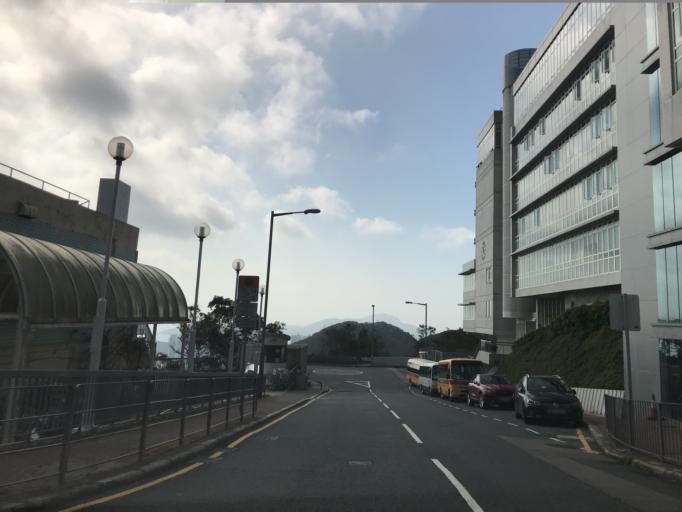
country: HK
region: Central and Western
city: Central
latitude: 22.2659
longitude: 114.1613
